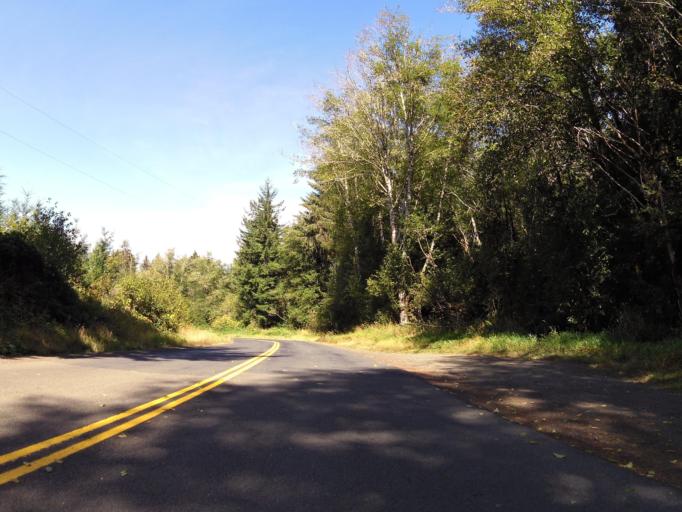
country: US
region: Washington
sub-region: Wahkiakum County
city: Cathlamet
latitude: 46.1766
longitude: -123.5278
